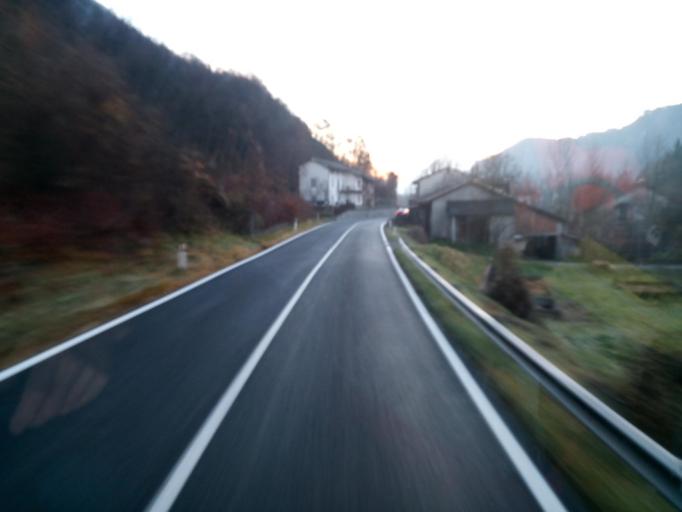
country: IT
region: Friuli Venezia Giulia
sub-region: Provincia di Udine
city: Lauco
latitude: 46.4121
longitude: 12.9441
